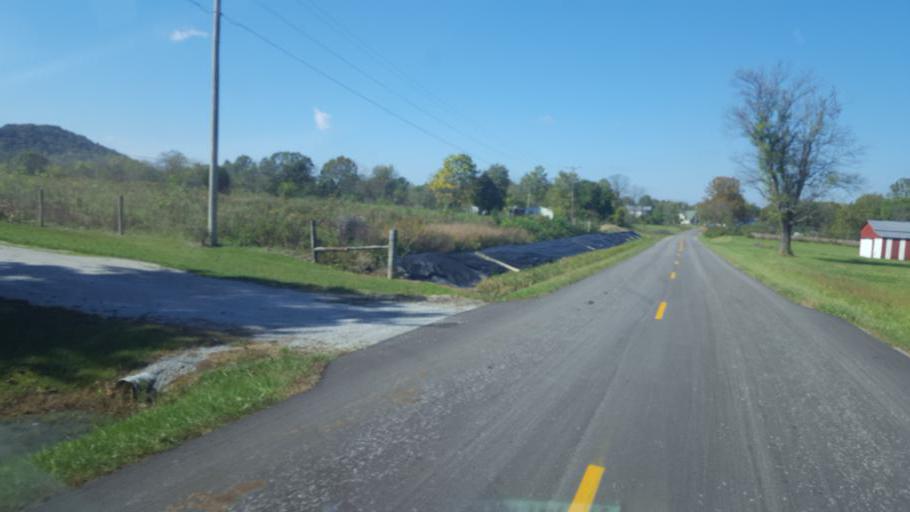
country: US
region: Kentucky
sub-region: Fleming County
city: Flemingsburg
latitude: 38.4714
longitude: -83.5903
